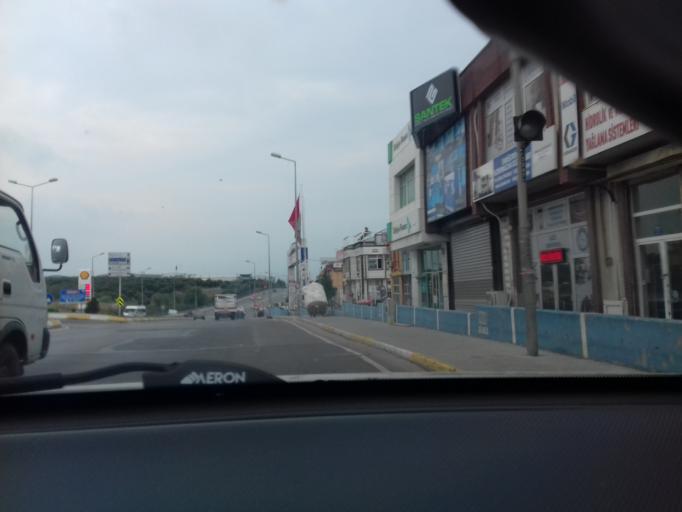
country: TR
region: Istanbul
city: Icmeler
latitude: 40.8821
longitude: 29.3470
